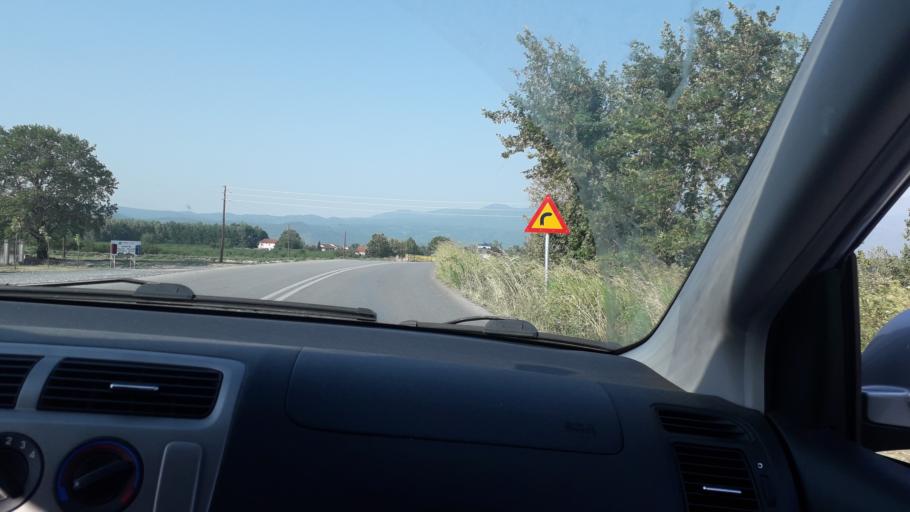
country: GR
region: Central Macedonia
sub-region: Nomos Pellis
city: Aridaia
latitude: 40.9618
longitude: 22.0494
